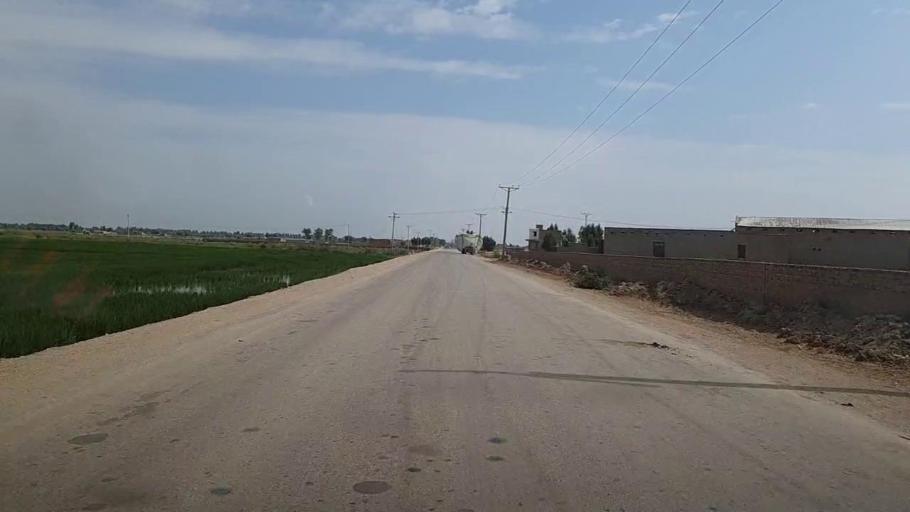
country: PK
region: Sindh
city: Thul
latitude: 28.2533
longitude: 68.7806
